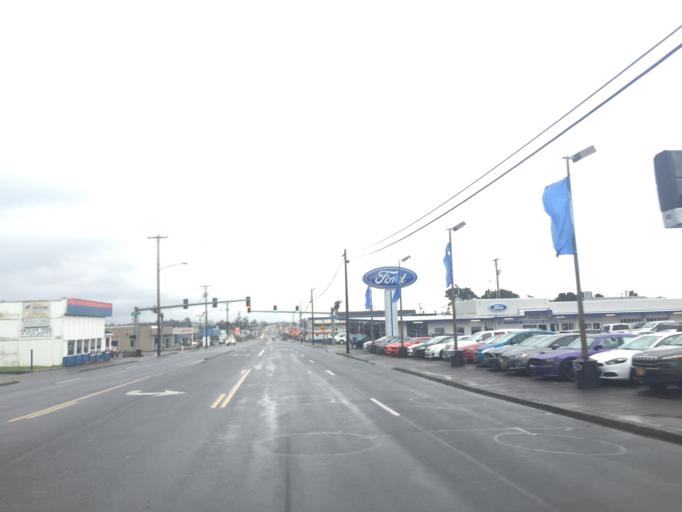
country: US
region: Oregon
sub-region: Lincoln County
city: Newport
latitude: 44.6455
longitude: -124.0531
